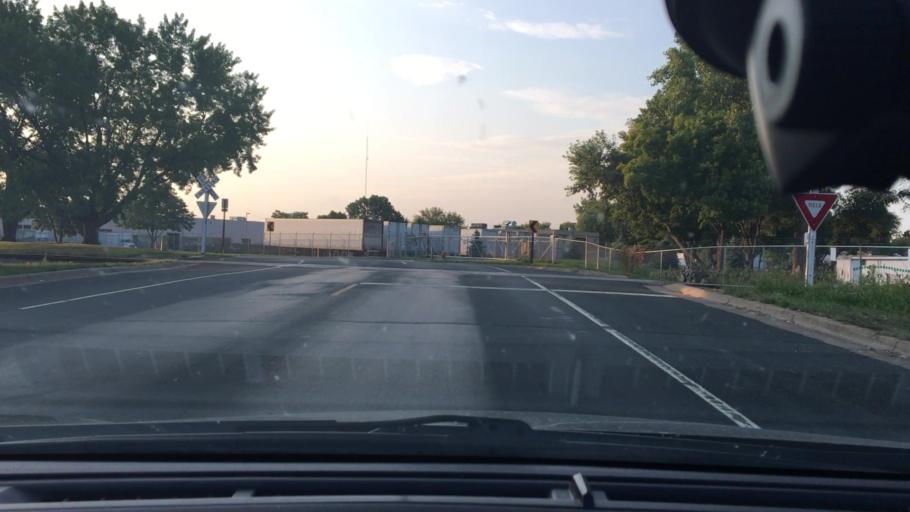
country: US
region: Minnesota
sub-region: Hennepin County
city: New Hope
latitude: 44.9891
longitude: -93.3972
